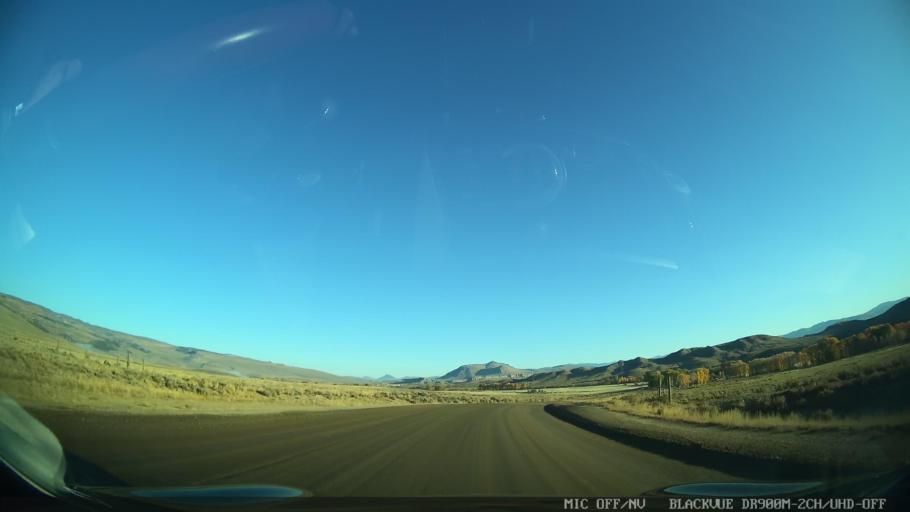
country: US
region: Colorado
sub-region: Grand County
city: Kremmling
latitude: 40.0247
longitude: -106.3893
